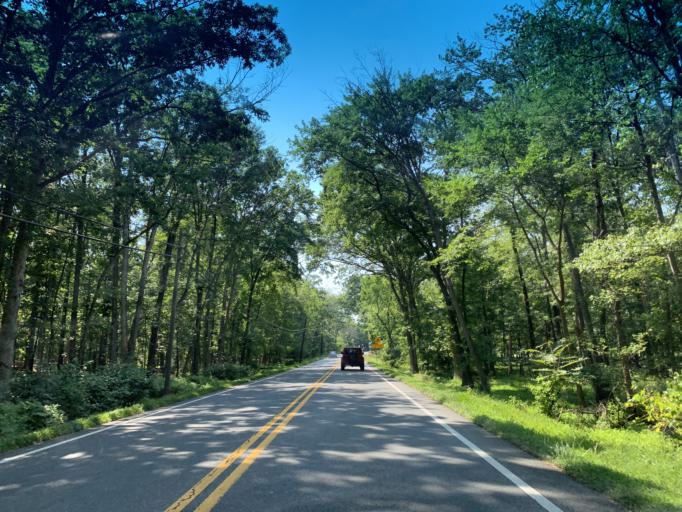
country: US
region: Maryland
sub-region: Montgomery County
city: Poolesville
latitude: 39.1274
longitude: -77.3814
